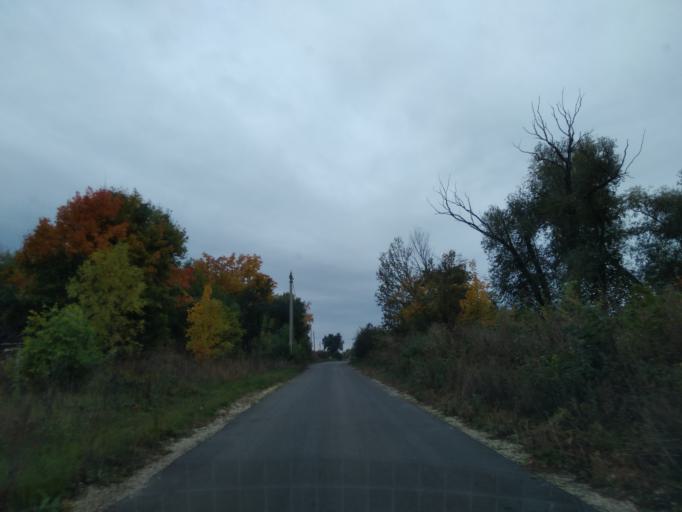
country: RU
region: Lipetsk
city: Zadonsk
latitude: 52.2919
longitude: 38.9466
